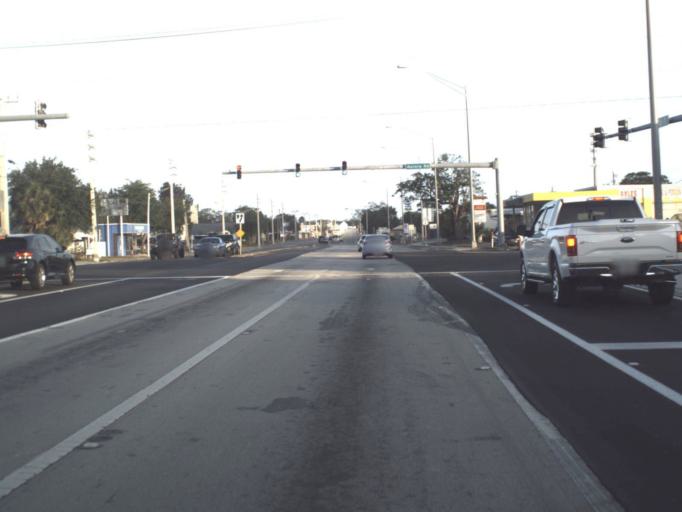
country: US
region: Florida
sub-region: Brevard County
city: Indian Harbour Beach
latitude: 28.1353
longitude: -80.6335
